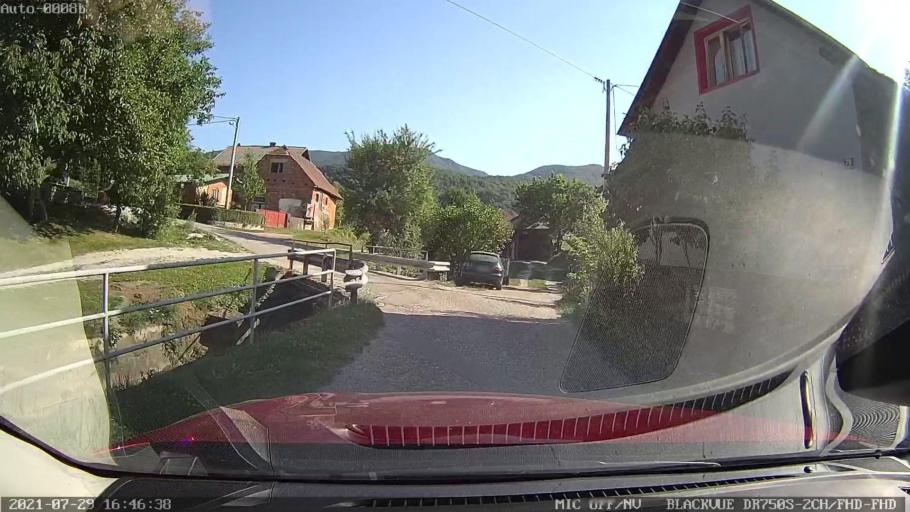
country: HR
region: Varazdinska
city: Ivanec
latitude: 46.2182
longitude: 16.1271
